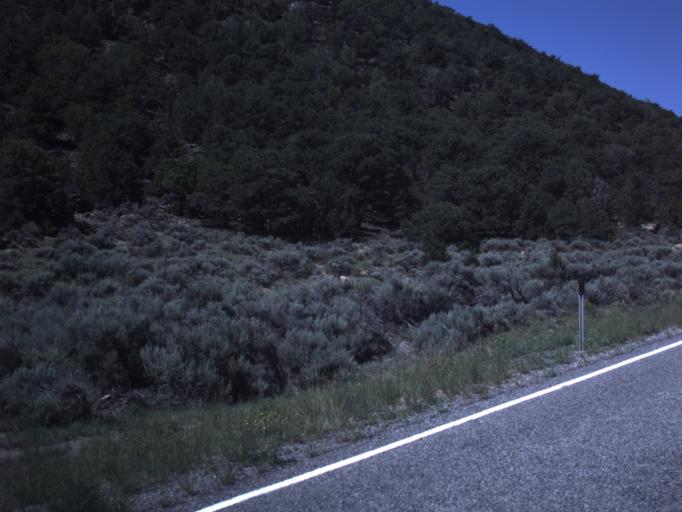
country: US
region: Utah
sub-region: Wayne County
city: Loa
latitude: 38.7567
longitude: -111.4033
